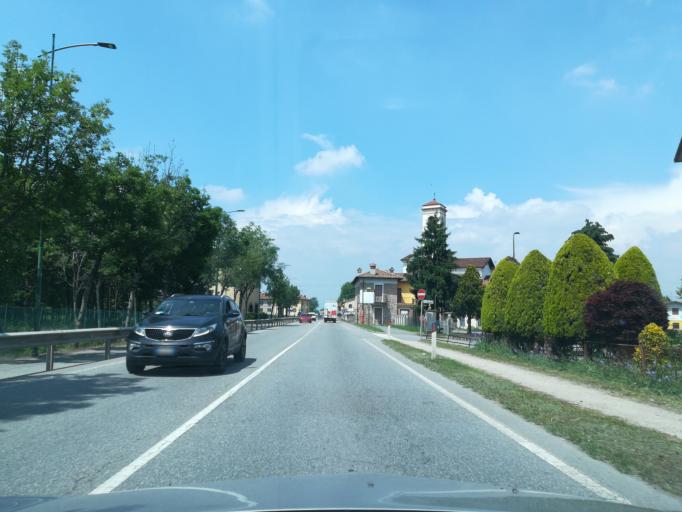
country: IT
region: Lombardy
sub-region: Provincia di Bergamo
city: Cavernago
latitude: 45.6290
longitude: 9.7663
